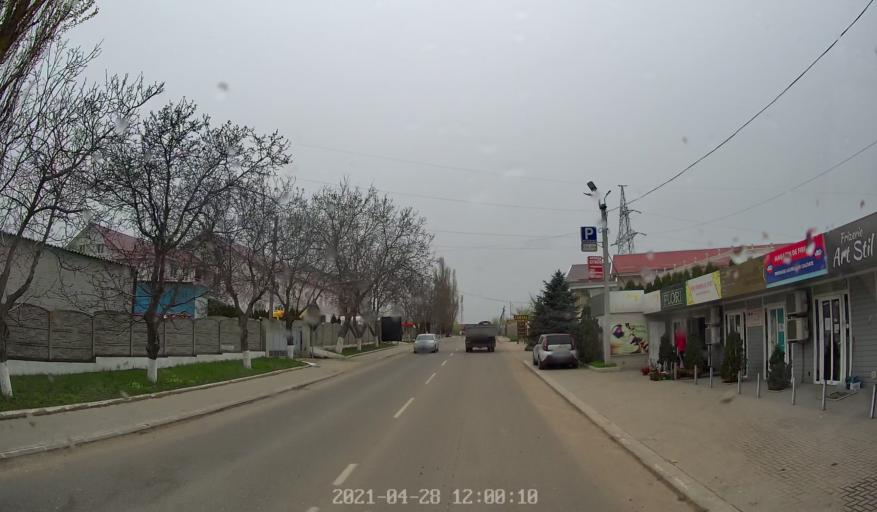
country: MD
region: Chisinau
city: Chisinau
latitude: 46.9844
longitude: 28.9309
